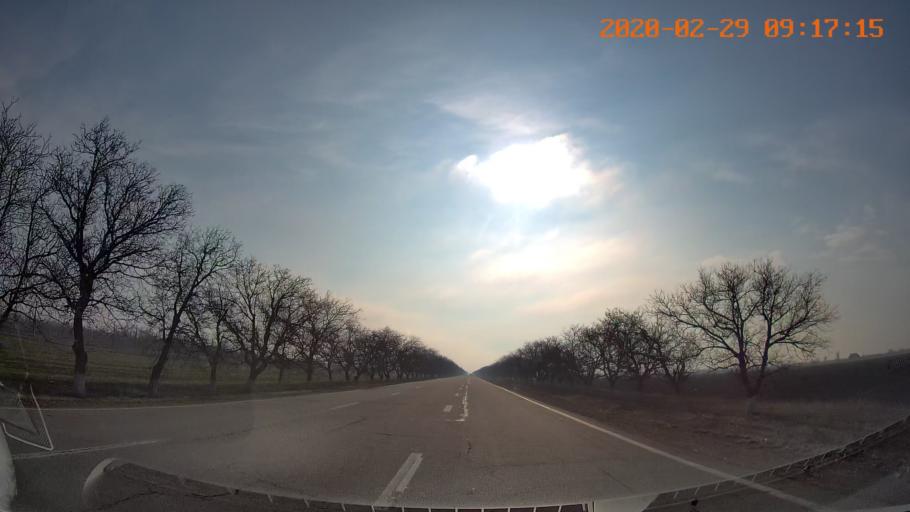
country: MD
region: Telenesti
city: Pervomaisc
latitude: 46.7846
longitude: 29.9009
